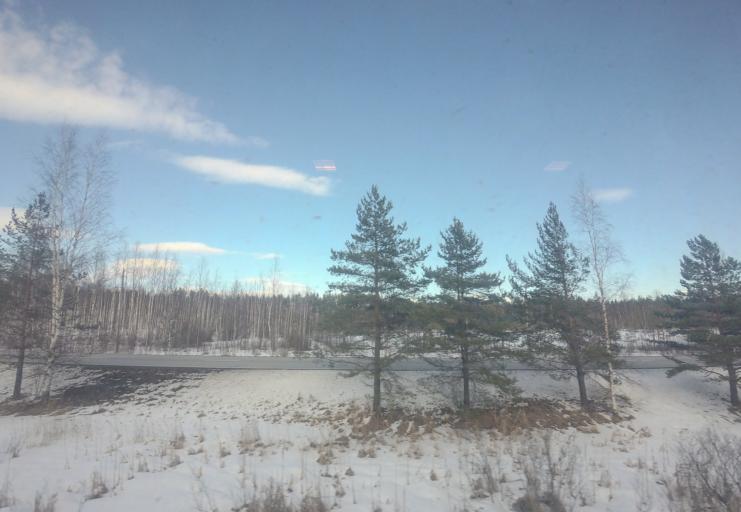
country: FI
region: Southern Savonia
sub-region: Savonlinna
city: Punkaharju
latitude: 61.7887
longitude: 29.3438
